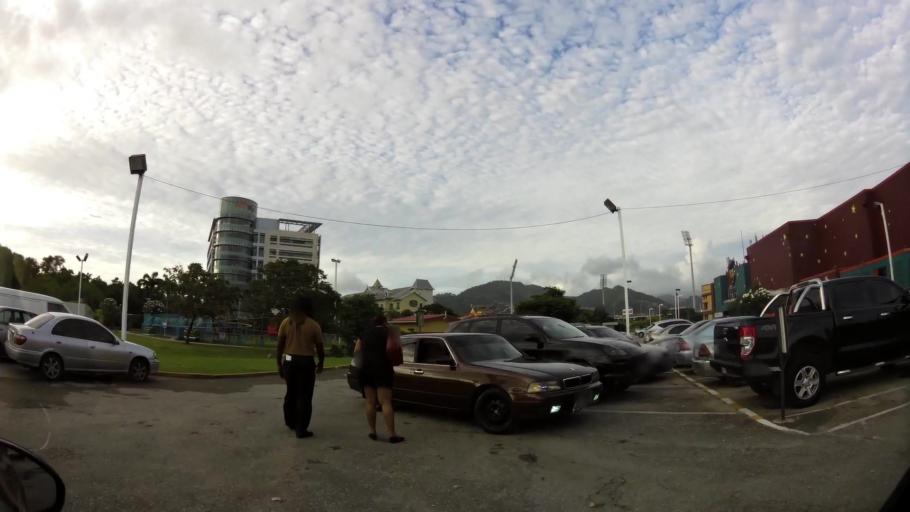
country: TT
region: City of Port of Spain
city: Mucurapo
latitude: 10.6584
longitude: -61.5333
